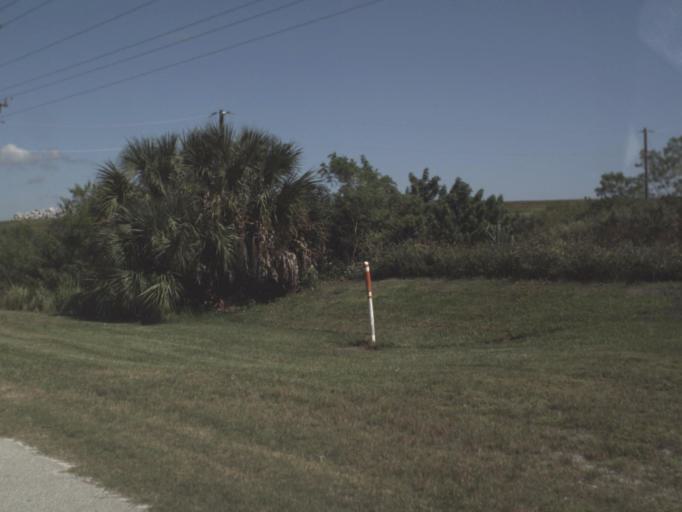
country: US
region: Florida
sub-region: Glades County
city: Moore Haven
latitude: 26.8824
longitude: -81.1225
